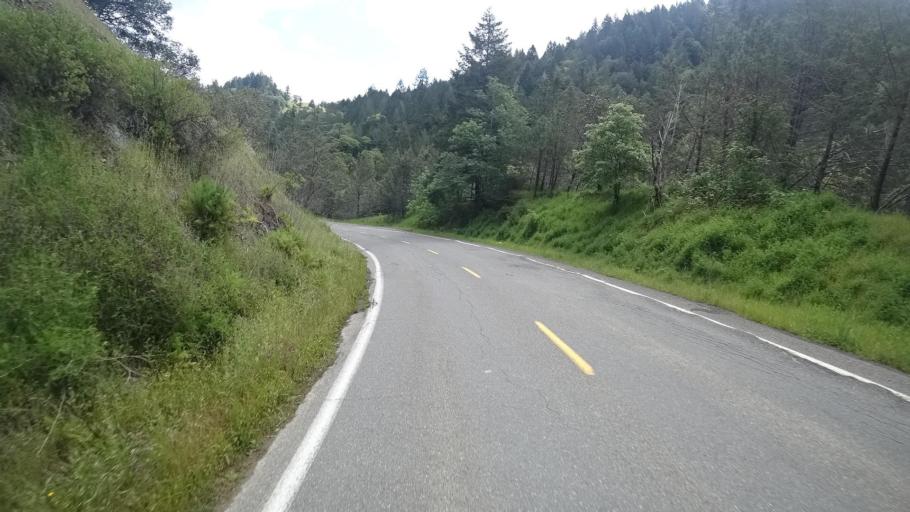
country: US
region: California
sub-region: Humboldt County
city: Redway
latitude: 40.1261
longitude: -123.8695
